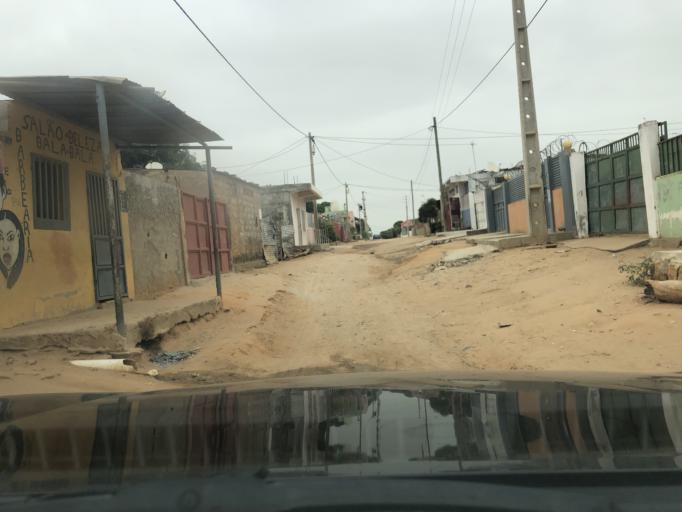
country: AO
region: Luanda
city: Luanda
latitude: -8.9379
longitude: 13.2348
